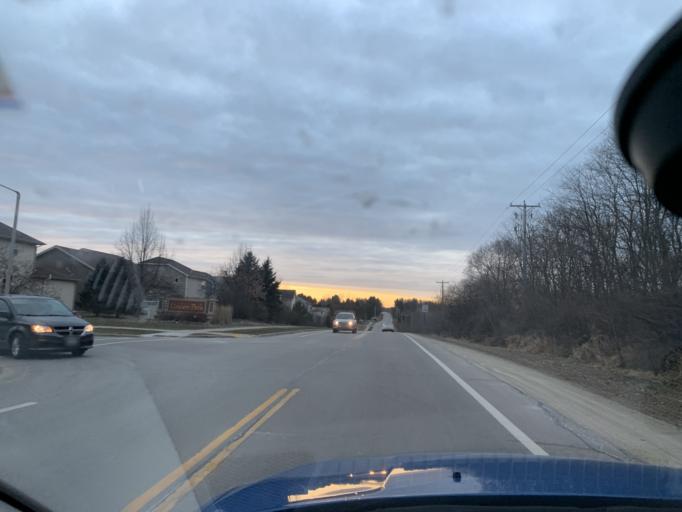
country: US
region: Wisconsin
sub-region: Dane County
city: Verona
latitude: 43.0457
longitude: -89.5426
